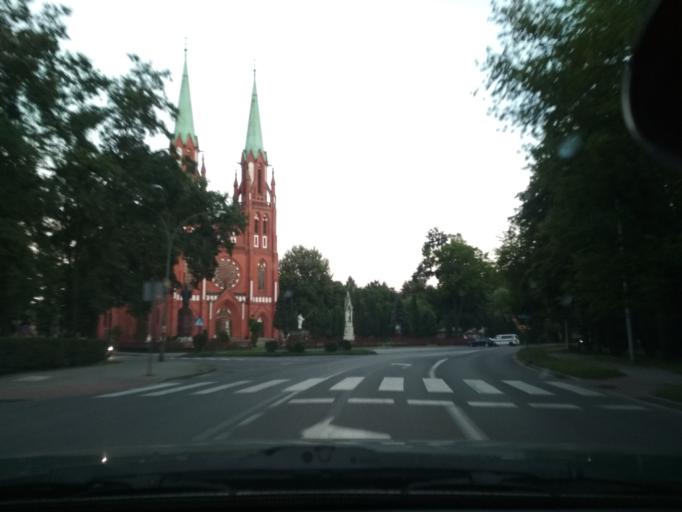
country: PL
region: Silesian Voivodeship
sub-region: Powiat zawiercianski
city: Zawiercie
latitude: 50.4891
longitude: 19.4247
